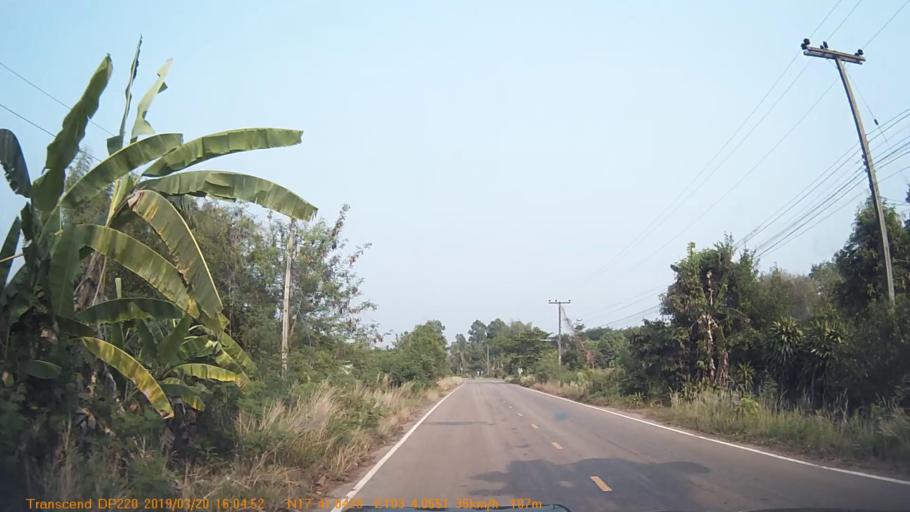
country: TH
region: Changwat Udon Thani
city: Phibun Rak
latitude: 17.6843
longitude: 103.0677
